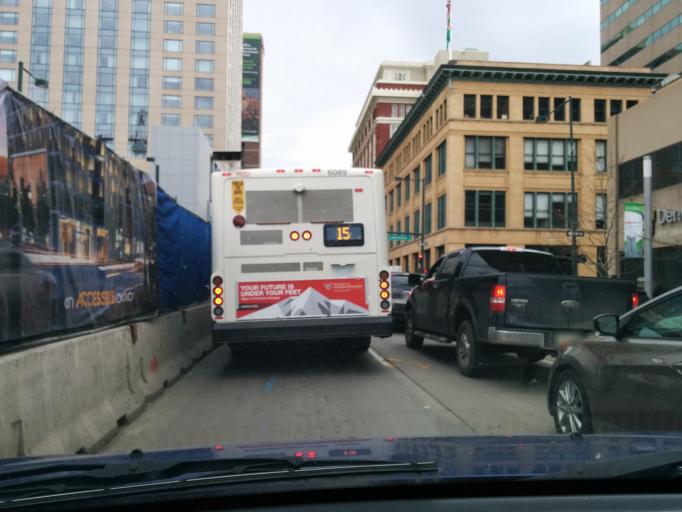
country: US
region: Colorado
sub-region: Denver County
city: Denver
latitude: 39.7469
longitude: -104.9993
